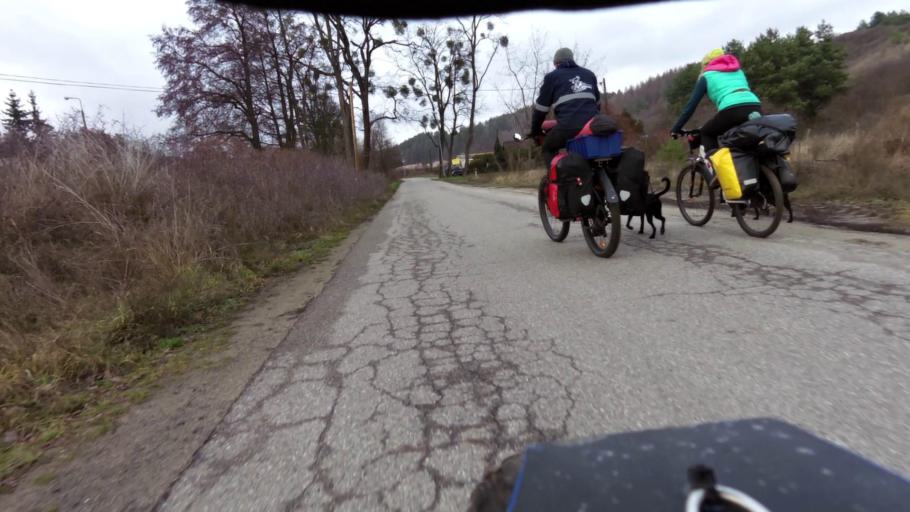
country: PL
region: Lubusz
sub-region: Powiat gorzowski
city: Jenin
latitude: 52.7076
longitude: 15.1323
